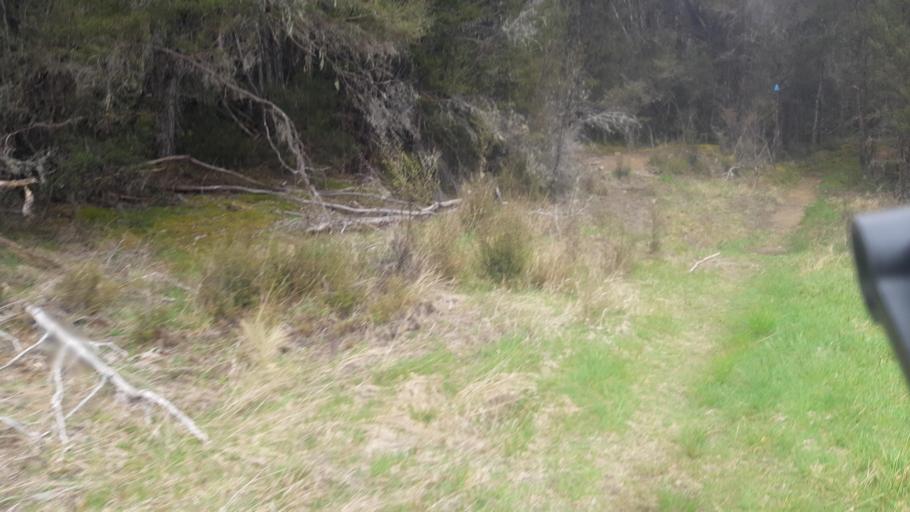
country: NZ
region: Tasman
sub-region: Tasman District
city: Wakefield
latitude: -41.7780
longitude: 172.8134
